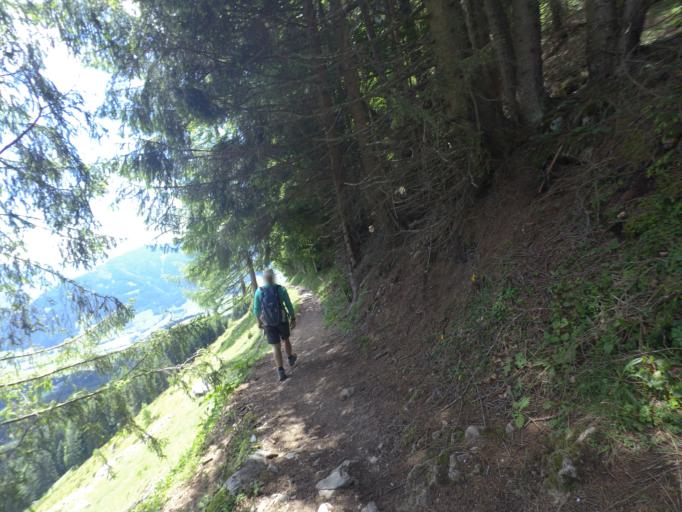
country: AT
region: Salzburg
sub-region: Politischer Bezirk Zell am See
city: Leogang
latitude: 47.4632
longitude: 12.7741
